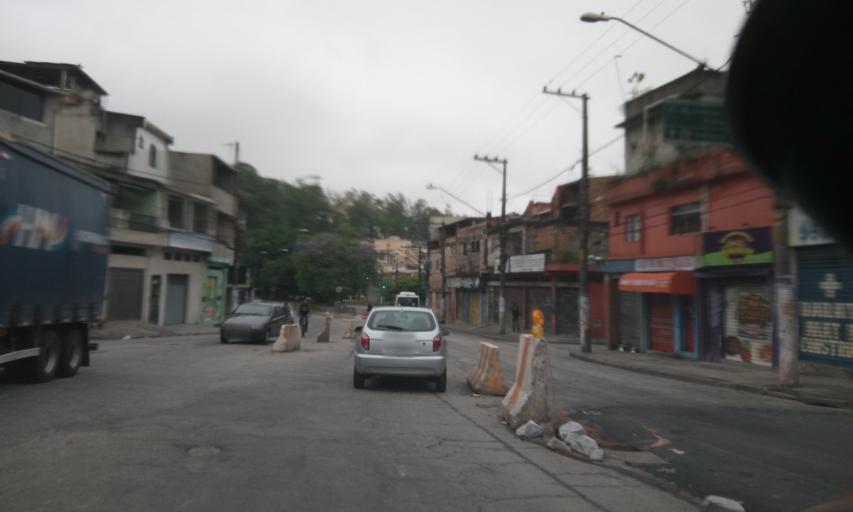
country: BR
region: Sao Paulo
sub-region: Sao Bernardo Do Campo
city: Sao Bernardo do Campo
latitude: -23.7096
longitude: -46.5288
